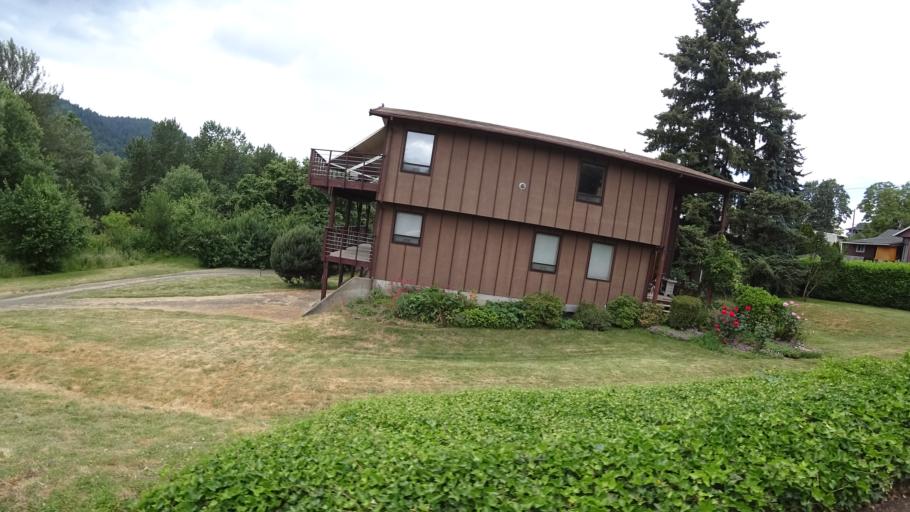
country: US
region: Oregon
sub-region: Washington County
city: West Haven
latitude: 45.5831
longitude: -122.7515
